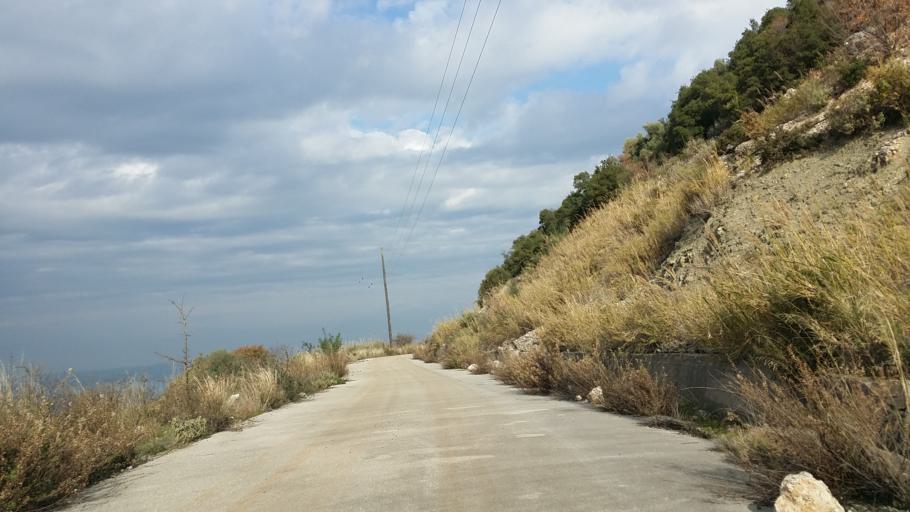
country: GR
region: West Greece
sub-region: Nomos Aitolias kai Akarnanias
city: Katouna
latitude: 38.8567
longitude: 21.0559
